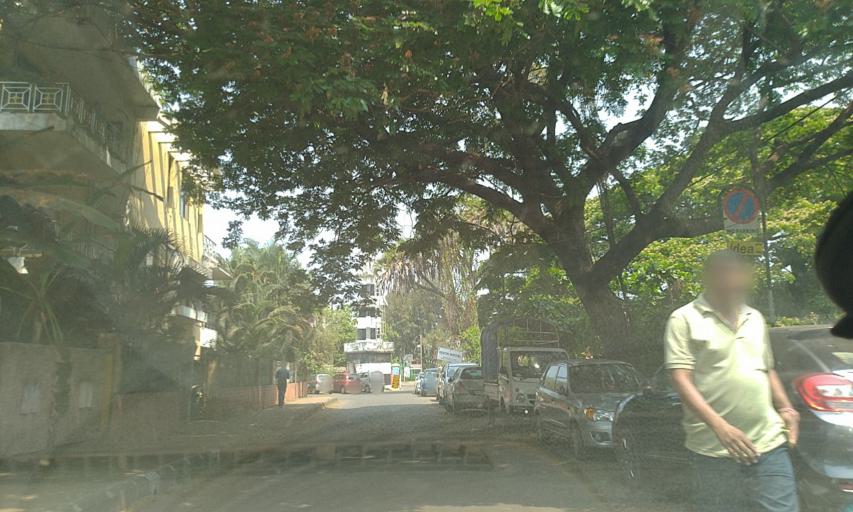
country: IN
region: Goa
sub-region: North Goa
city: Panaji
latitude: 15.4874
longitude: 73.8106
